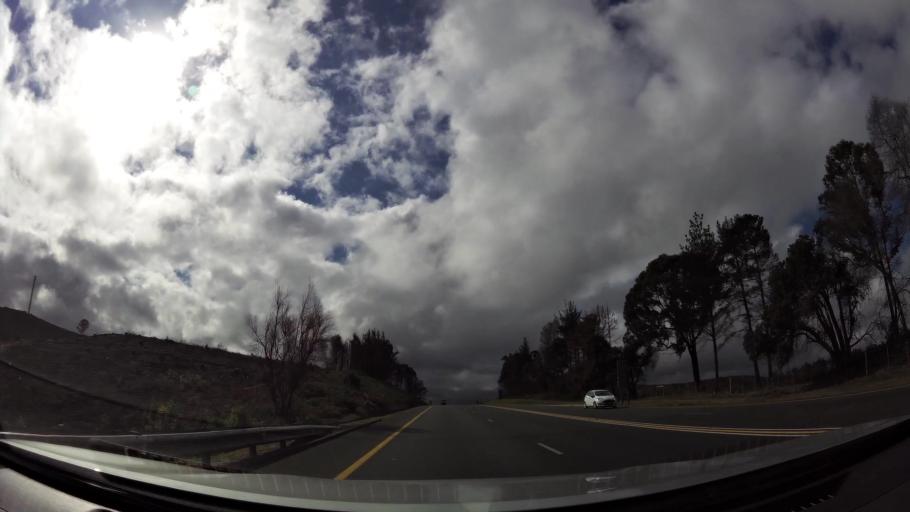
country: ZA
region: Western Cape
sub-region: Eden District Municipality
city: Knysna
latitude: -34.0378
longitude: 23.1218
